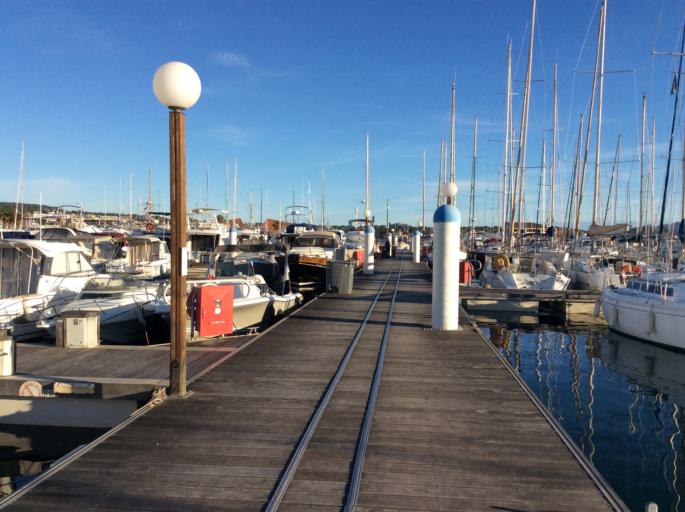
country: FR
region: Provence-Alpes-Cote d'Azur
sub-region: Departement du Var
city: Bandol
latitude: 43.1353
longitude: 5.7556
